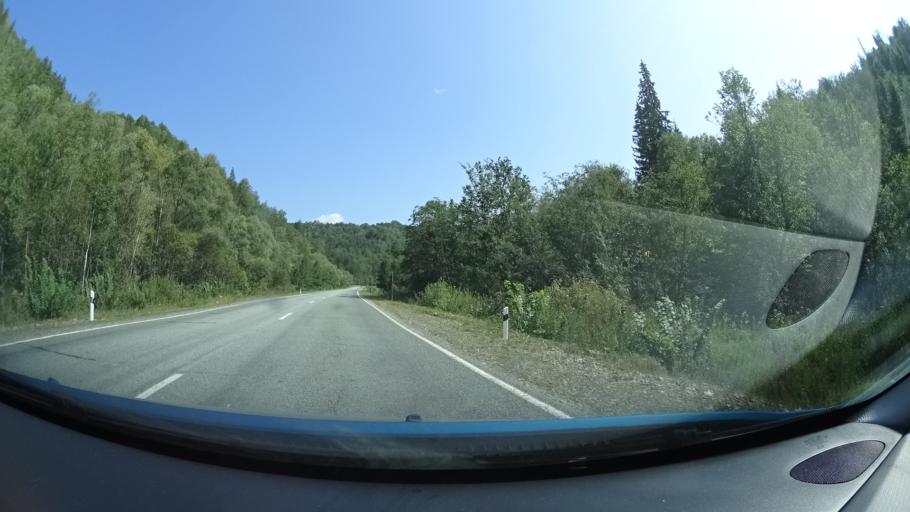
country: RU
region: Bashkortostan
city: Inzer
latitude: 54.3178
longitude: 57.1778
